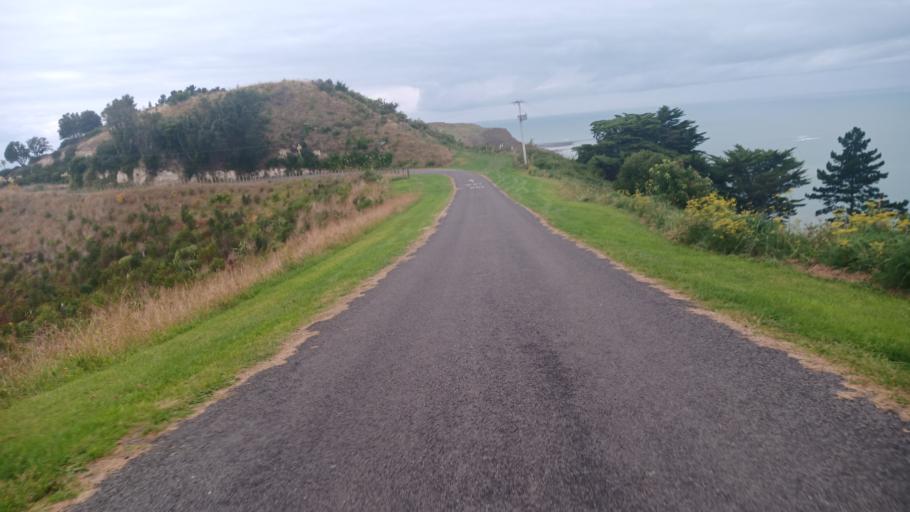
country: NZ
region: Gisborne
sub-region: Gisborne District
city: Gisborne
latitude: -38.6800
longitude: 178.0319
